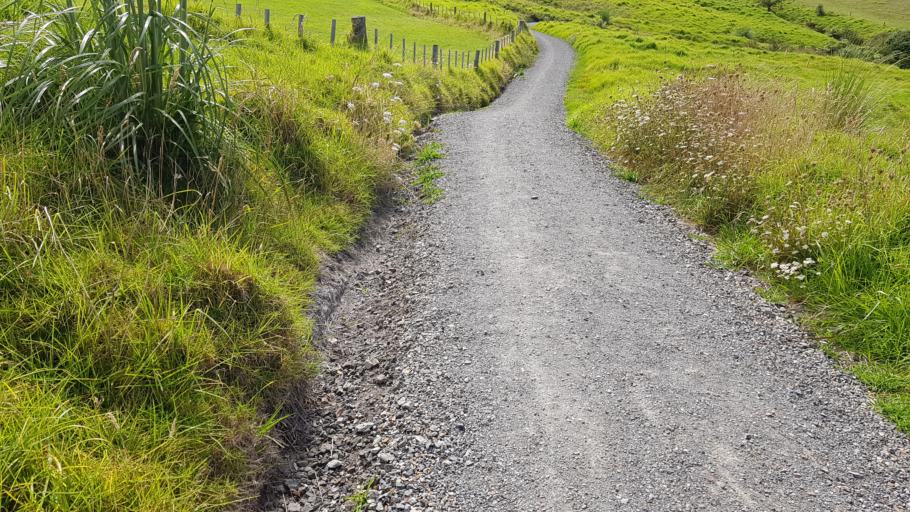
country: NZ
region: Auckland
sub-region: Auckland
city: Rothesay Bay
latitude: -36.6708
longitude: 174.7468
